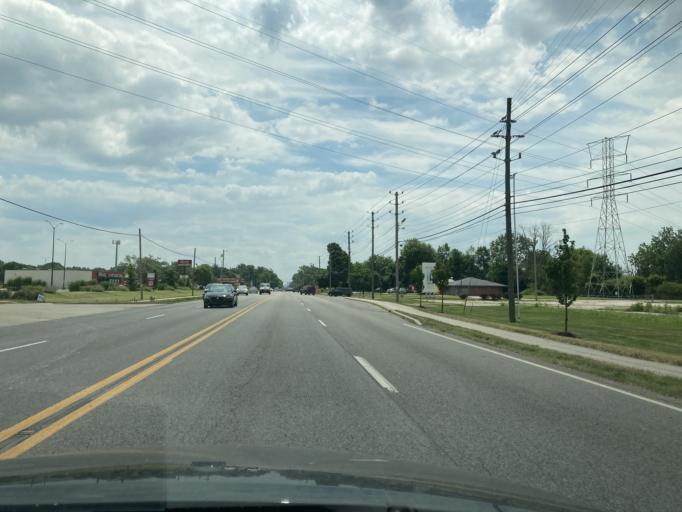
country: US
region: Indiana
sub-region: Marion County
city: Meridian Hills
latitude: 39.8825
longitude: -86.2087
